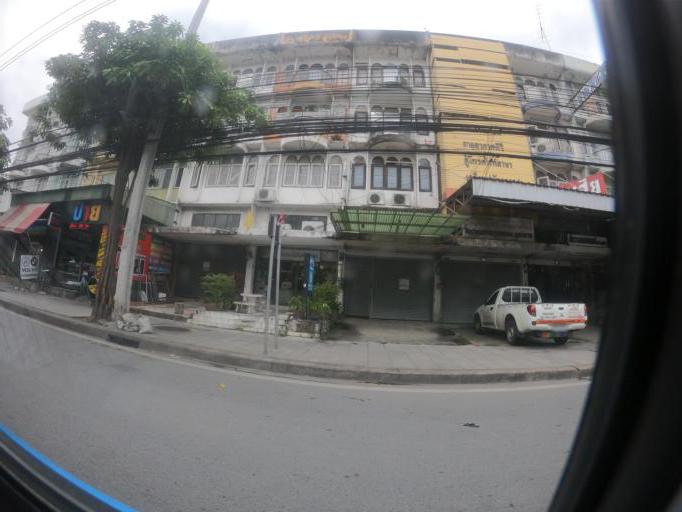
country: TH
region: Bangkok
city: Suan Luang
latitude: 13.7304
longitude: 100.6536
